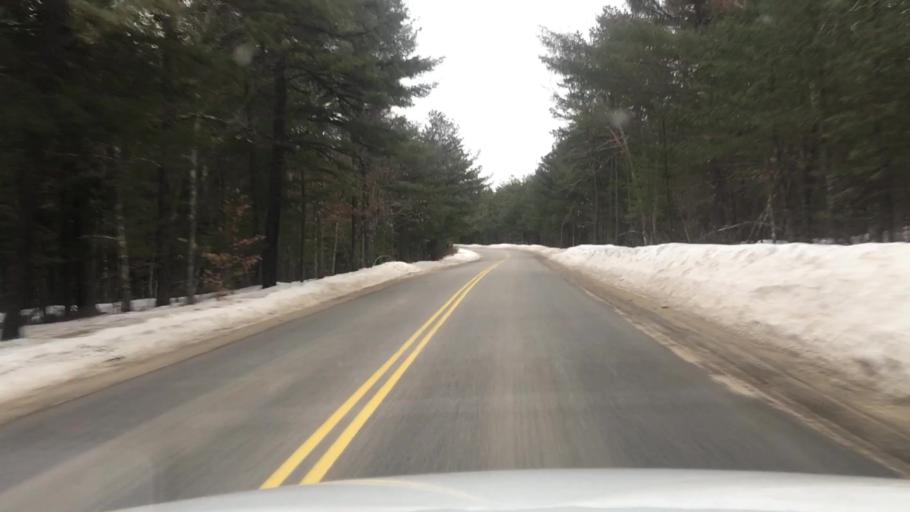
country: US
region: Maine
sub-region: York County
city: Newfield
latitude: 43.6016
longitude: -70.8788
